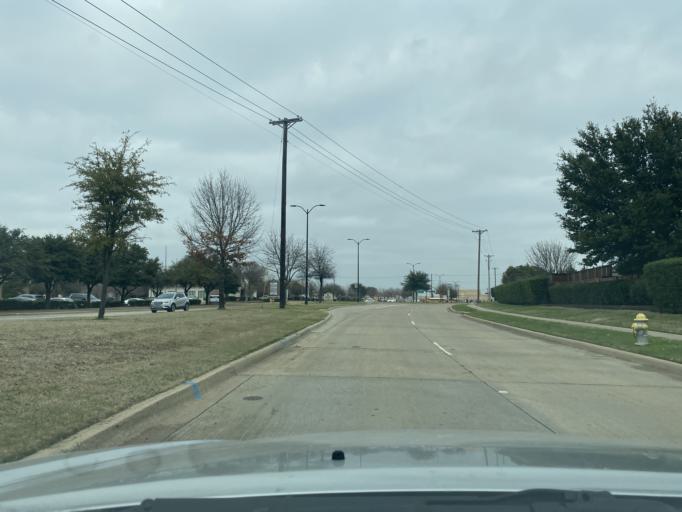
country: US
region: Texas
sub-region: Collin County
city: Frisco
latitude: 33.1164
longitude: -96.8019
